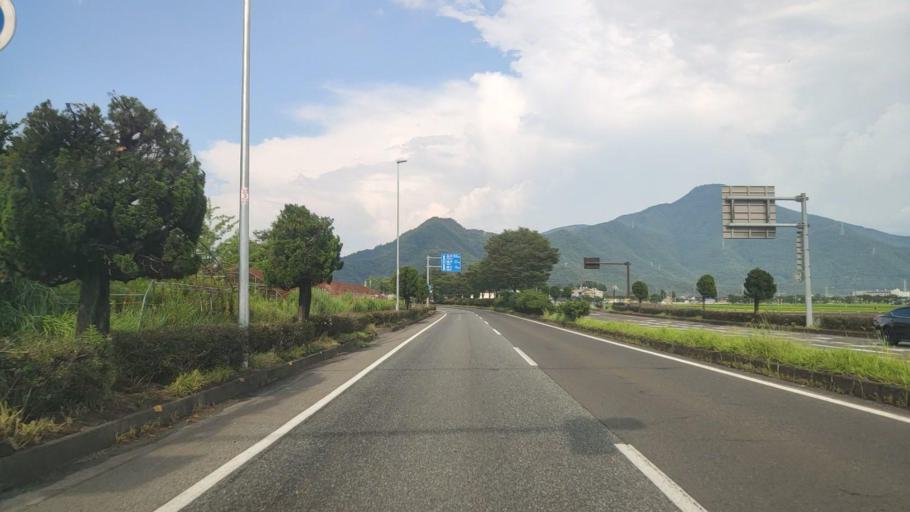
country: JP
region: Fukui
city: Takefu
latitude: 35.8729
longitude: 136.1569
